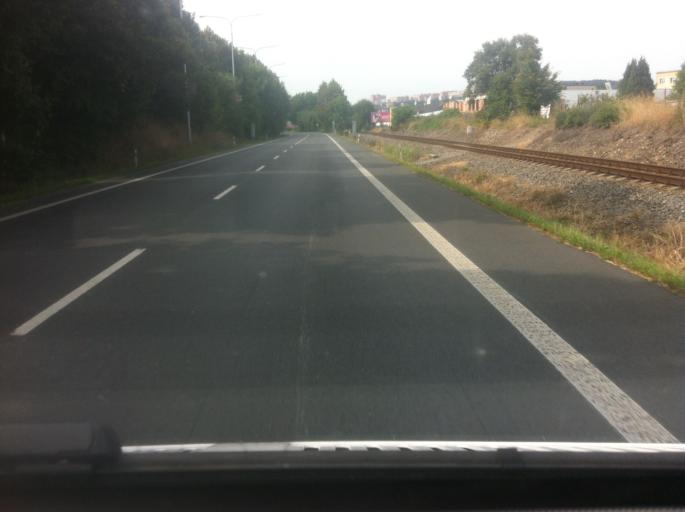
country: CZ
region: Zlin
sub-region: Okres Zlin
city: Zlin
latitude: 49.2238
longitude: 17.6998
